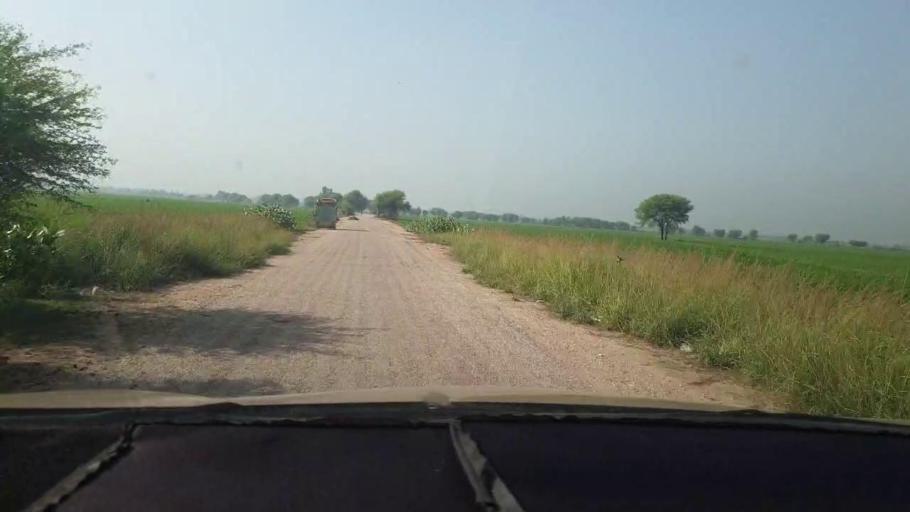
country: PK
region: Sindh
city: Kambar
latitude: 27.6281
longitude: 68.0895
